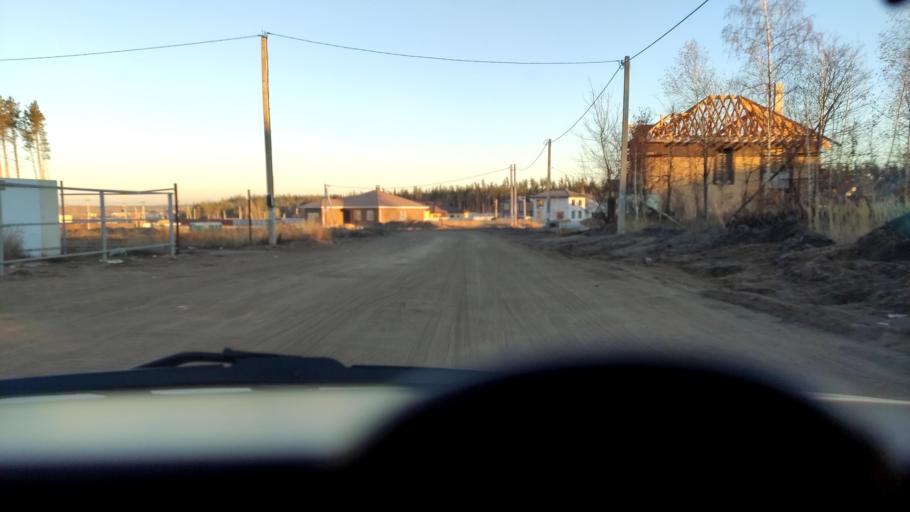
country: RU
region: Voronezj
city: Podgornoye
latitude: 51.7455
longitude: 39.1422
